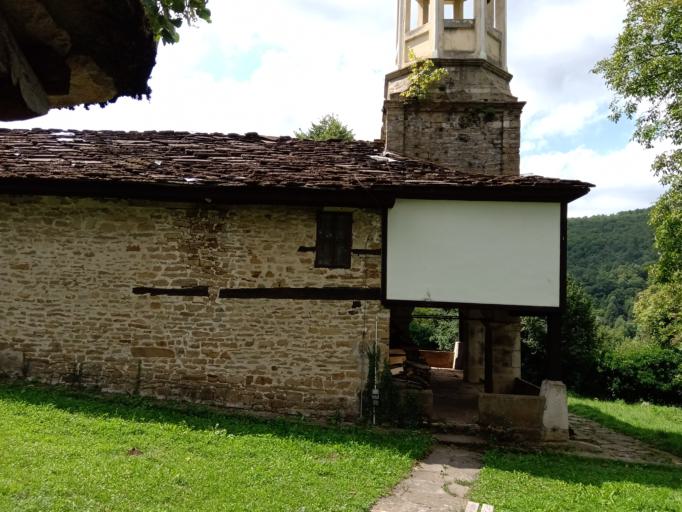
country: BG
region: Gabrovo
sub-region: Obshtina Tryavna
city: Tryavna
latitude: 42.8746
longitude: 25.4254
